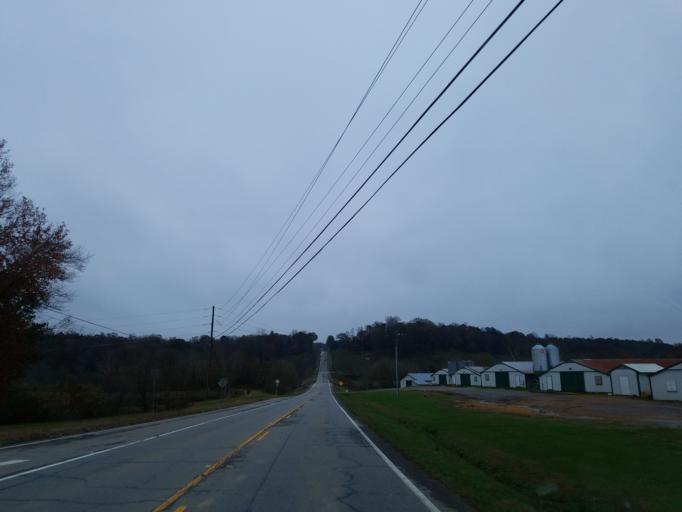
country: US
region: Georgia
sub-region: Pickens County
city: Nelson
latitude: 34.4008
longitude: -84.4314
